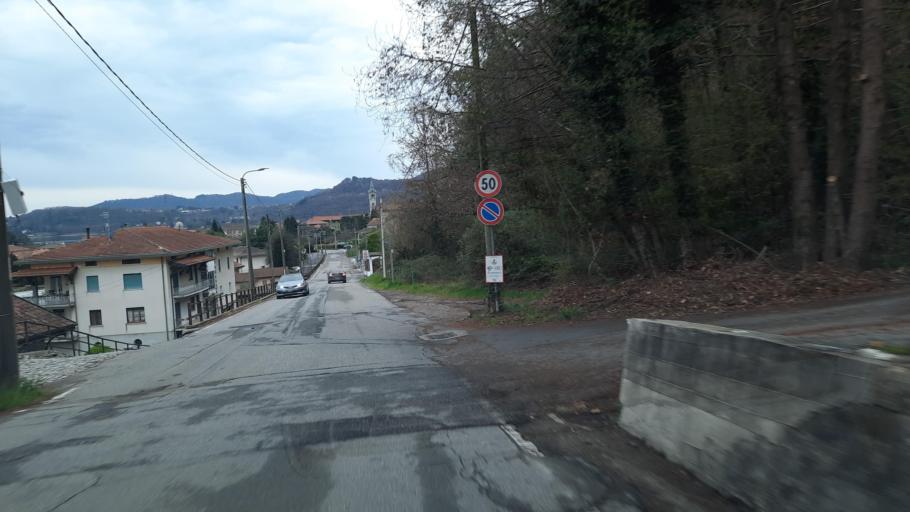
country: IT
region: Piedmont
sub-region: Provincia di Novara
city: Pella
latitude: 45.8055
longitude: 8.3847
